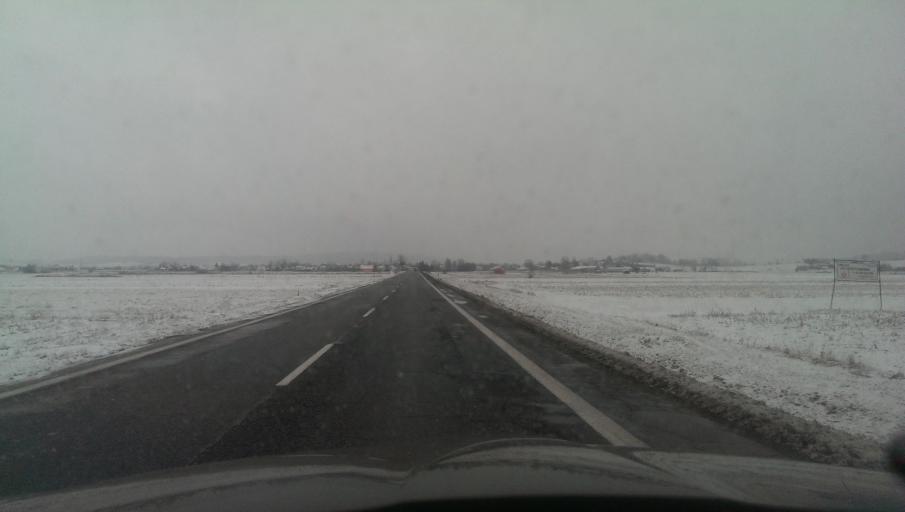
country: PL
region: Subcarpathian Voivodeship
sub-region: Powiat sanocki
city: Zarszyn
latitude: 49.5830
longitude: 21.9894
